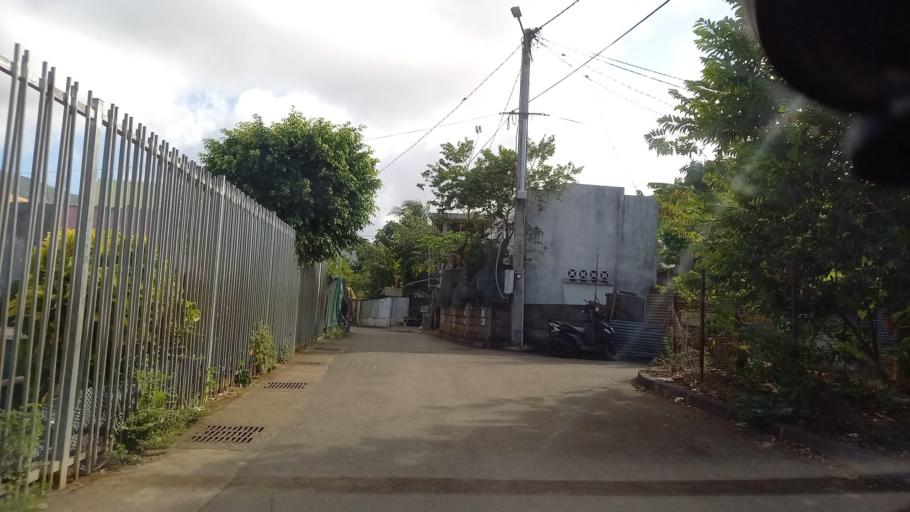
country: YT
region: Bandrele
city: Bandrele
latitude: -12.9109
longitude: 45.1949
